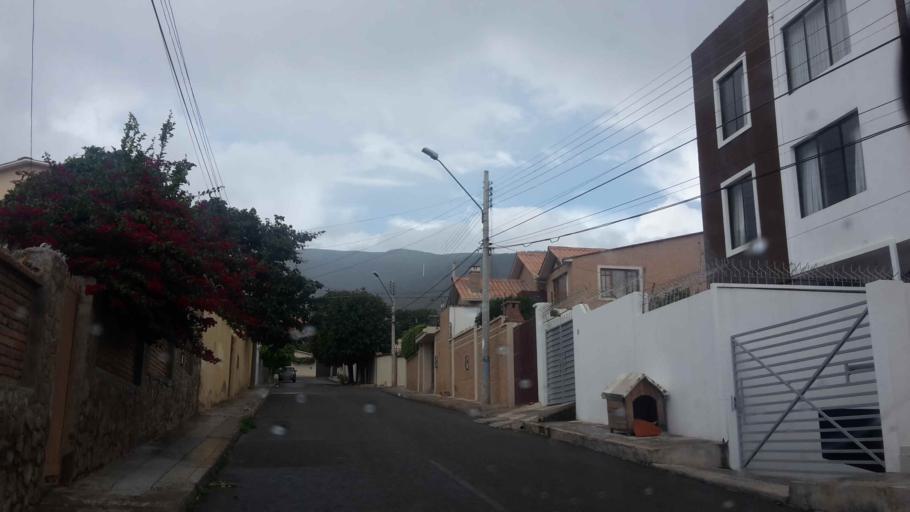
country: BO
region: Cochabamba
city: Cochabamba
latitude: -17.3587
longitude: -66.1572
